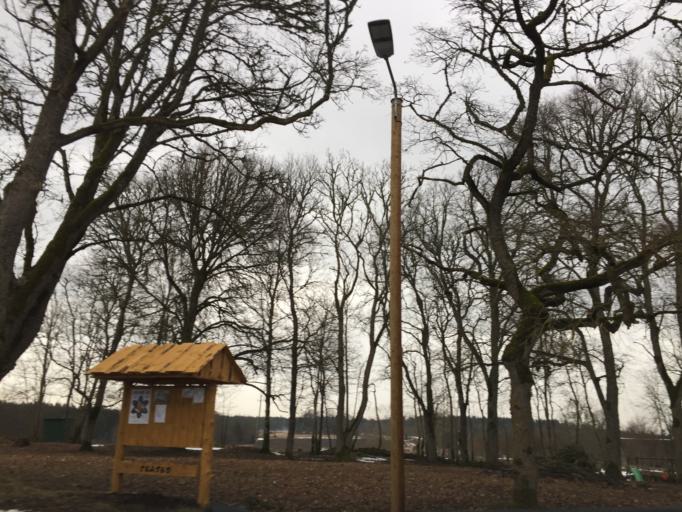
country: EE
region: Saare
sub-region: Orissaare vald
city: Orissaare
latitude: 58.5526
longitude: 22.7745
